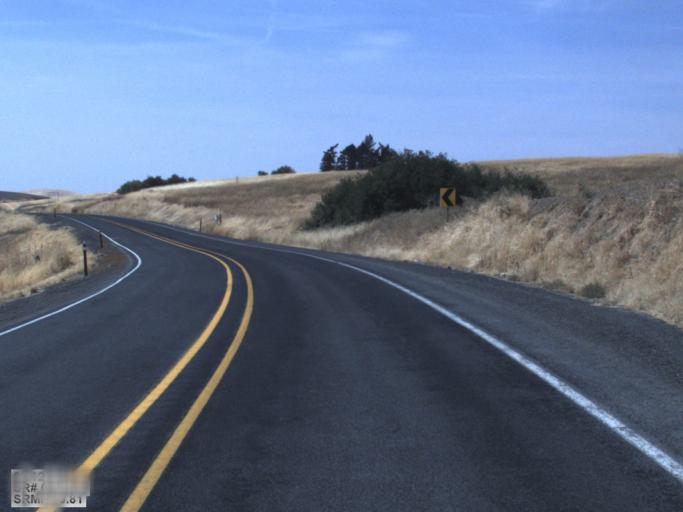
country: US
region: Idaho
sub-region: Benewah County
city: Plummer
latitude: 47.2321
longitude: -117.0969
